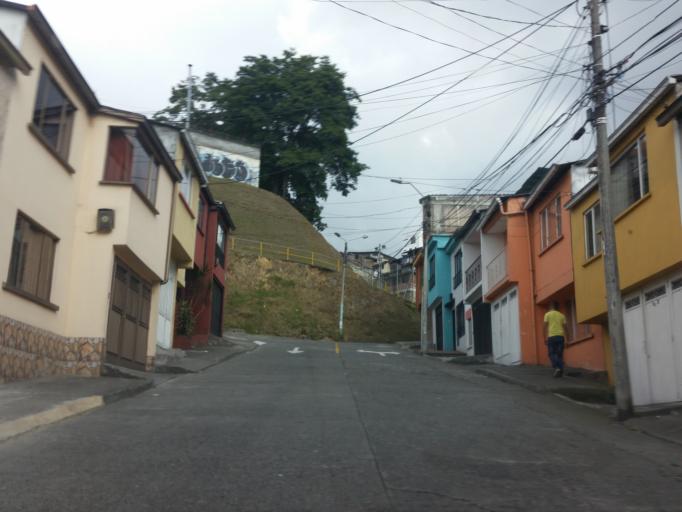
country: CO
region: Caldas
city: Manizales
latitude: 5.0618
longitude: -75.5051
